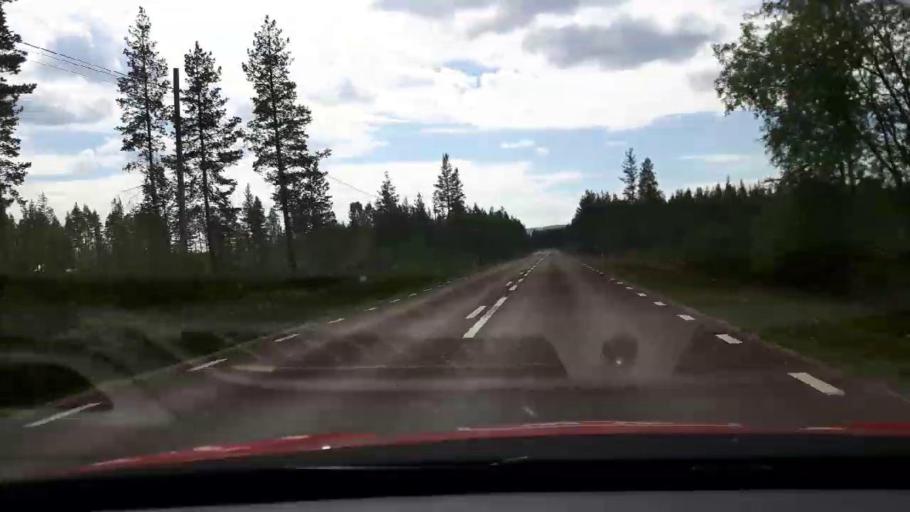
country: SE
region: Jaemtland
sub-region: Harjedalens Kommun
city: Sveg
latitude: 62.1233
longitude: 14.9708
